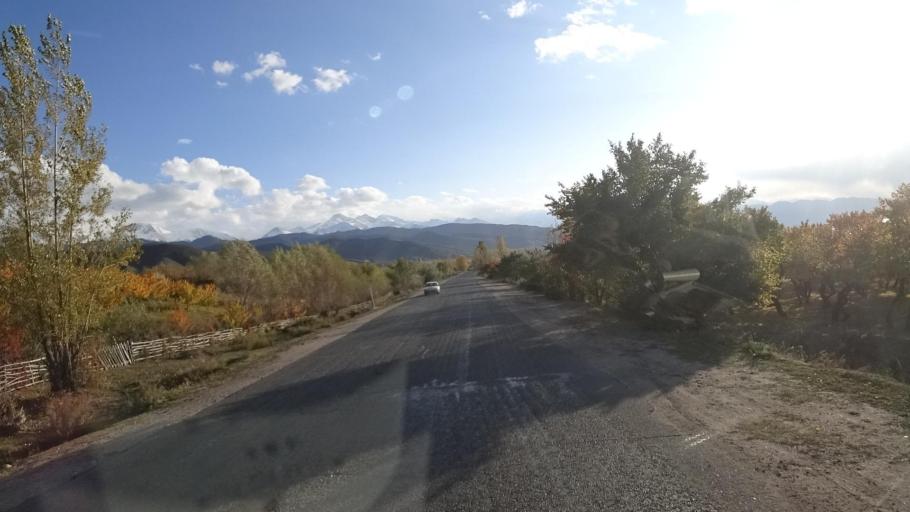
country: KG
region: Ysyk-Koel
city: Pokrovka
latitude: 42.2303
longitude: 77.7154
